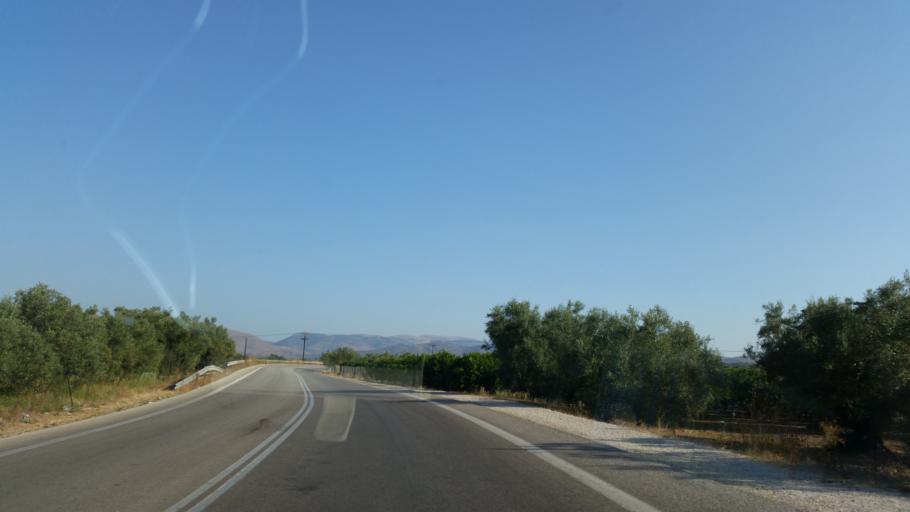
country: GR
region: Peloponnese
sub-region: Nomos Argolidos
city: Nea Tirins
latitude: 37.5958
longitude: 22.8289
